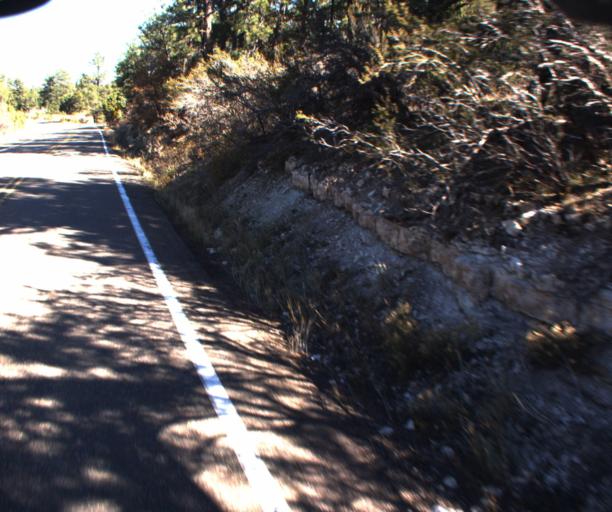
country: US
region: Arizona
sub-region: Coconino County
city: Fredonia
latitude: 36.7866
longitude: -112.2576
